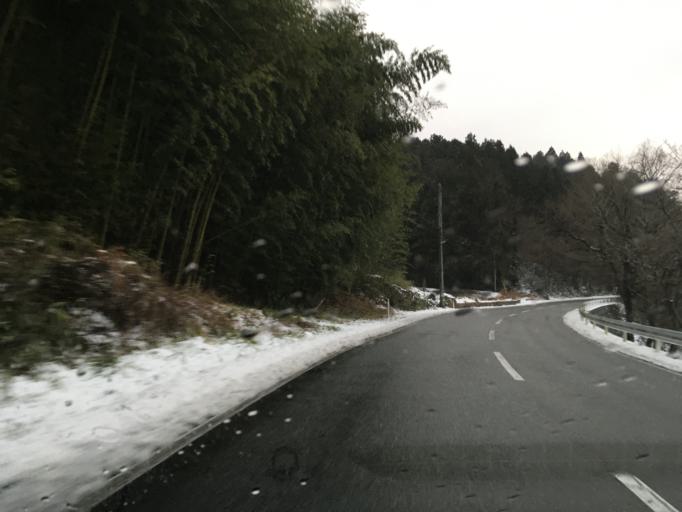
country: JP
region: Iwate
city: Ichinoseki
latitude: 38.8944
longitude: 141.2678
